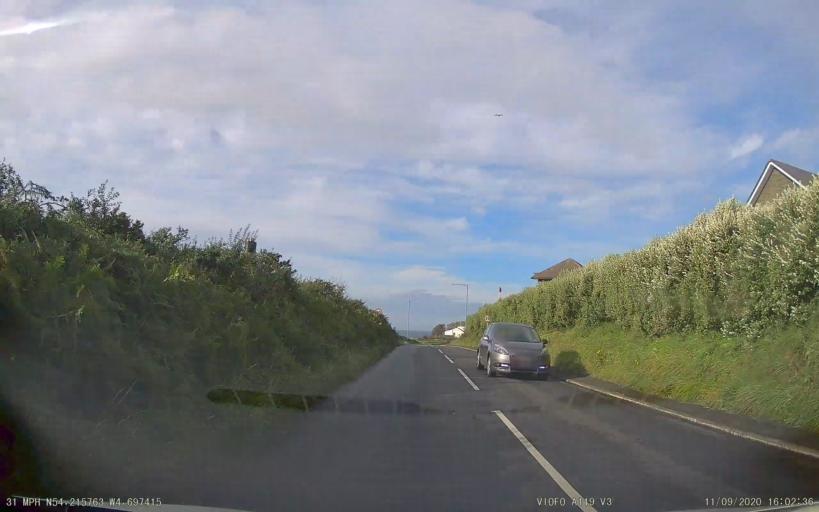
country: IM
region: Port Erin
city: Port Erin
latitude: 54.2158
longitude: -4.6974
